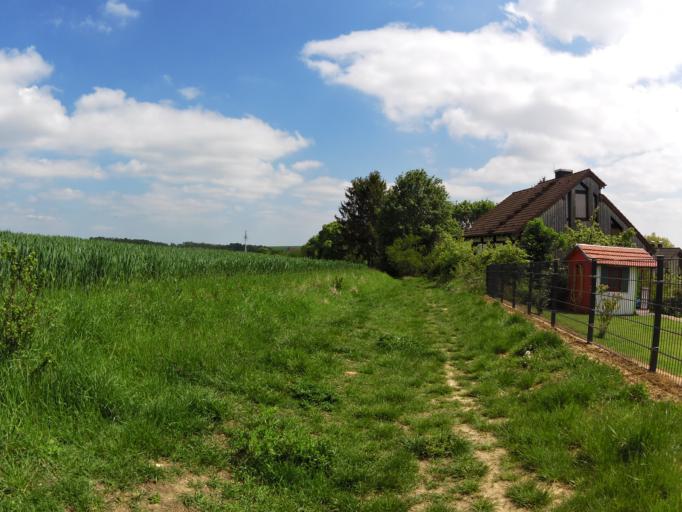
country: DE
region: Bavaria
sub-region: Regierungsbezirk Unterfranken
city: Reichenberg
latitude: 49.7353
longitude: 9.9073
